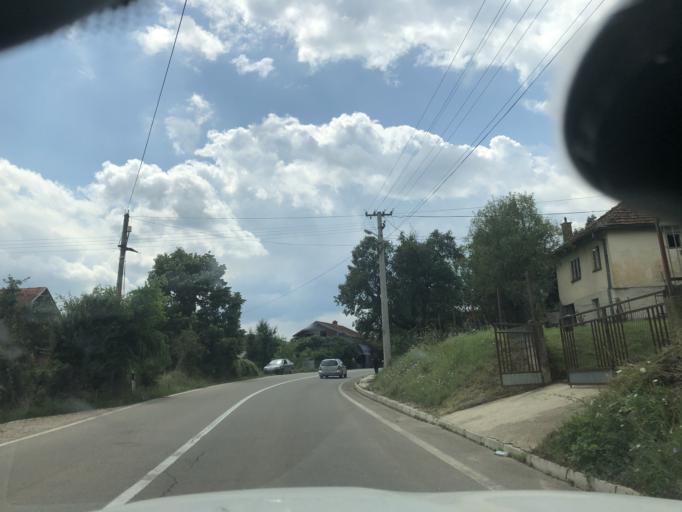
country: RS
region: Central Serbia
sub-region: Jablanicki Okrug
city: Medvega
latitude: 42.8321
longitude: 21.5848
